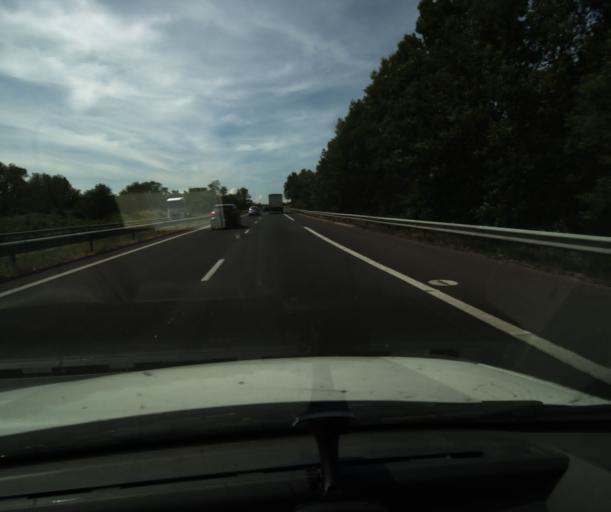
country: FR
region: Languedoc-Roussillon
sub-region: Departement de l'Aude
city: Villeneuve-la-Comptal
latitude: 43.2913
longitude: 1.9376
